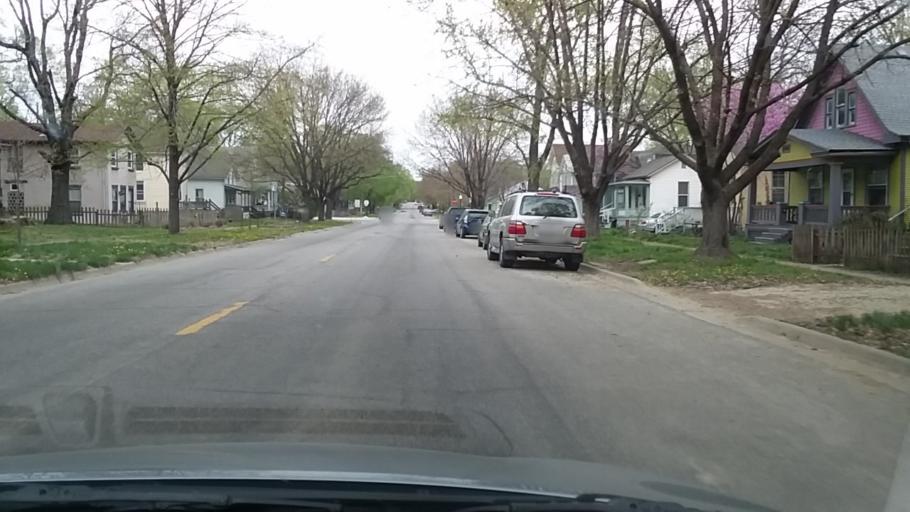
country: US
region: Kansas
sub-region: Douglas County
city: Lawrence
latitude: 38.9665
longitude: -95.2324
